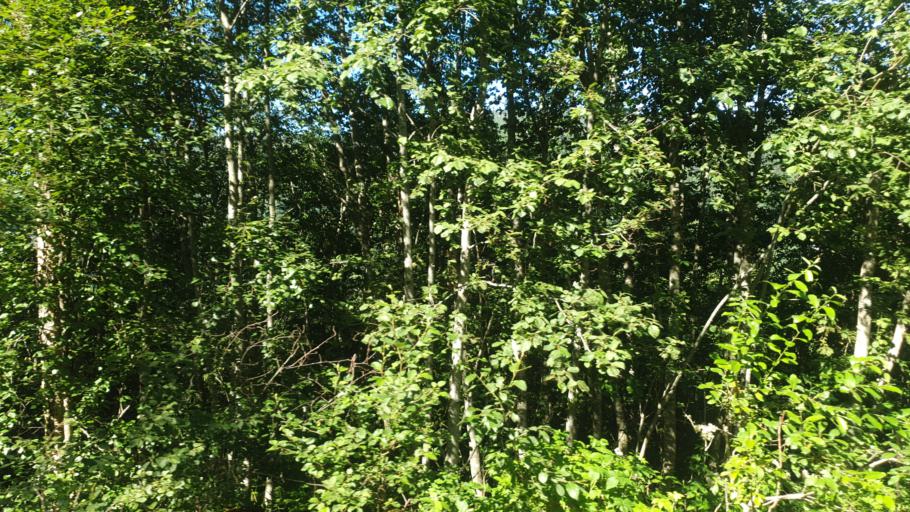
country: NO
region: Sor-Trondelag
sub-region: Meldal
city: Meldal
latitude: 63.1597
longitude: 9.7287
